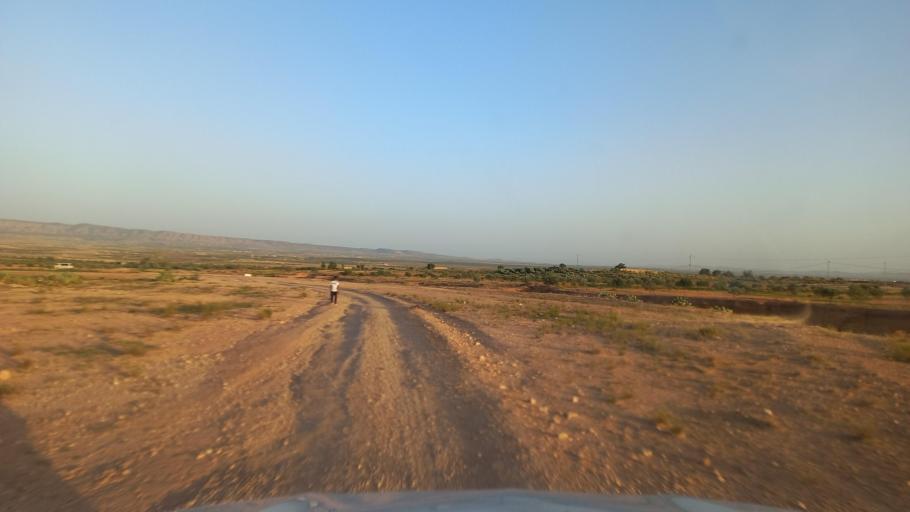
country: TN
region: Al Qasrayn
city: Sbiba
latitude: 35.3715
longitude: 9.0092
